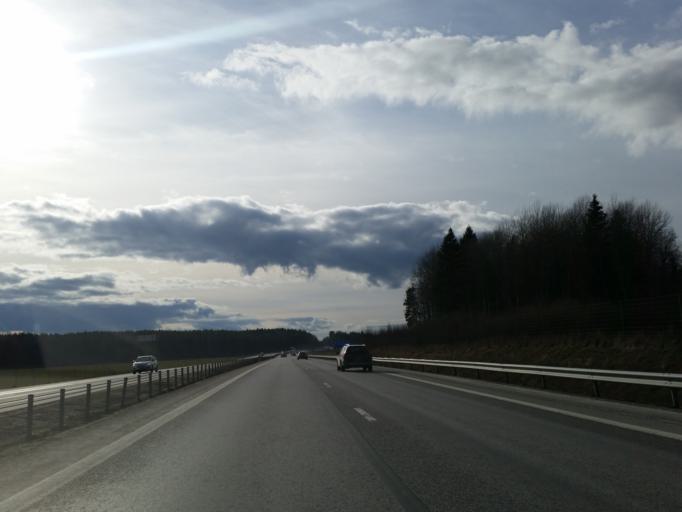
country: SE
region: Soedermanland
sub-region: Nykopings Kommun
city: Nykoping
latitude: 58.7467
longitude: 16.9537
